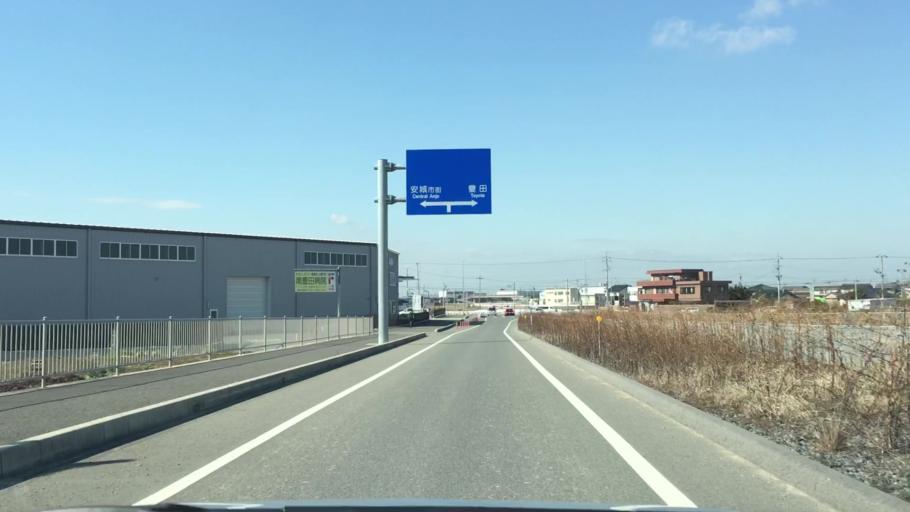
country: JP
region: Aichi
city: Anjo
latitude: 34.9940
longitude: 137.1129
